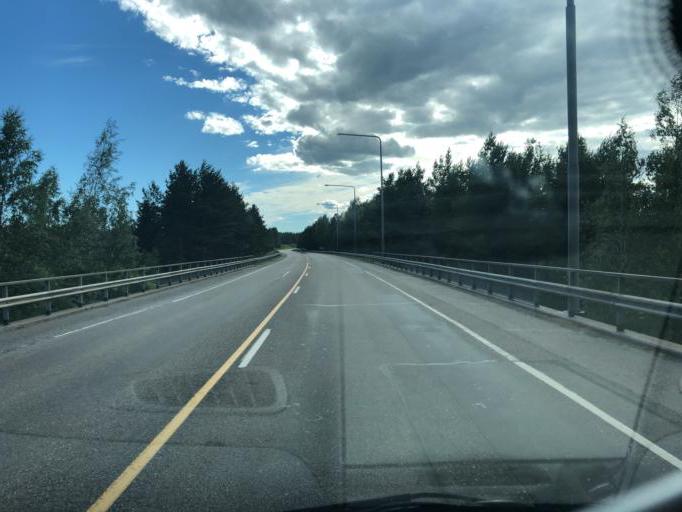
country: FI
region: Kymenlaakso
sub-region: Kouvola
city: Kouvola
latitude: 60.8715
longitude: 26.5956
